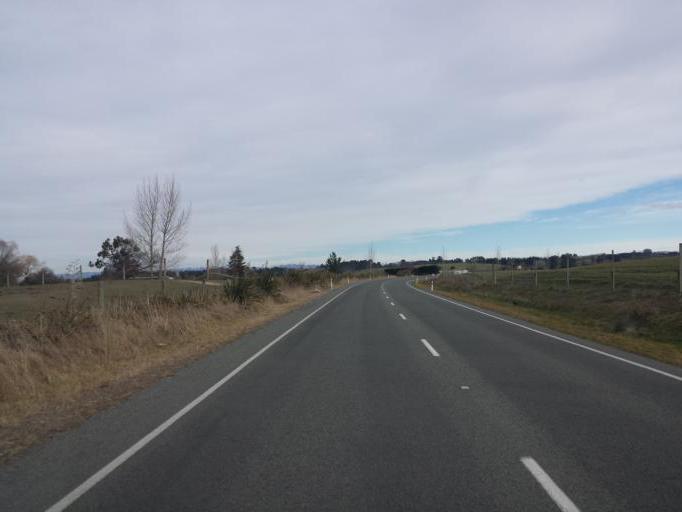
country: NZ
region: Canterbury
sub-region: Timaru District
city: Pleasant Point
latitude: -44.1212
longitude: 171.1965
